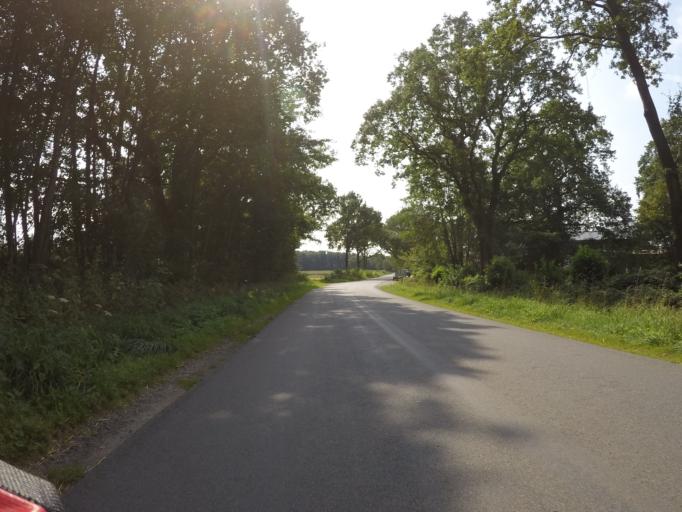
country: DE
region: Schleswig-Holstein
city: Kisdorf
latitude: 53.7769
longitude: 10.0210
